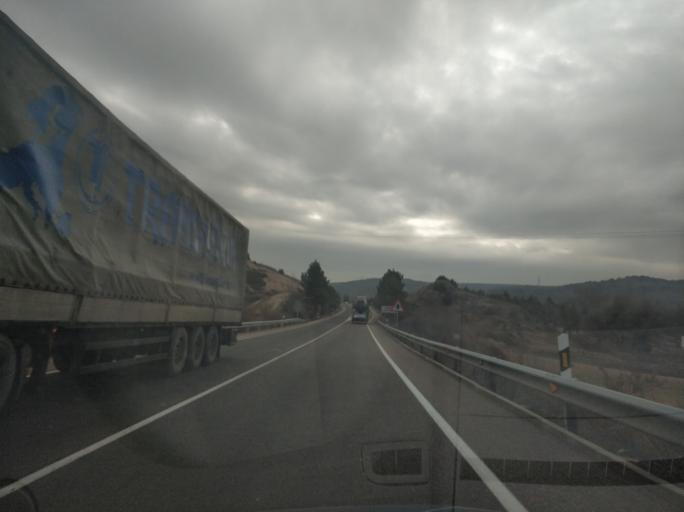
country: ES
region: Castille and Leon
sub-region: Provincia de Soria
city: Langa de Duero
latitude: 41.6234
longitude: -3.4547
